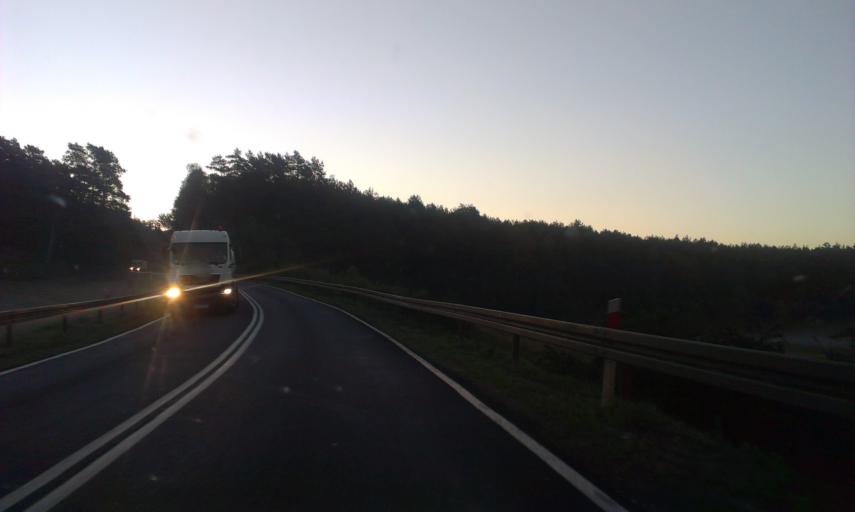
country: PL
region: Kujawsko-Pomorskie
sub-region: Powiat tucholski
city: Tuchola
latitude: 53.5544
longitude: 17.9031
